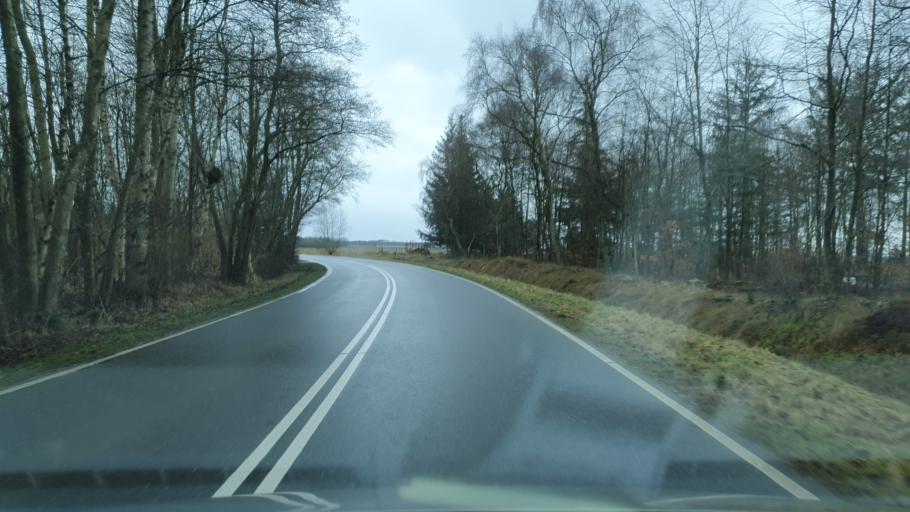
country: DK
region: North Denmark
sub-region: Jammerbugt Kommune
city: Fjerritslev
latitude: 57.1194
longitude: 9.1258
